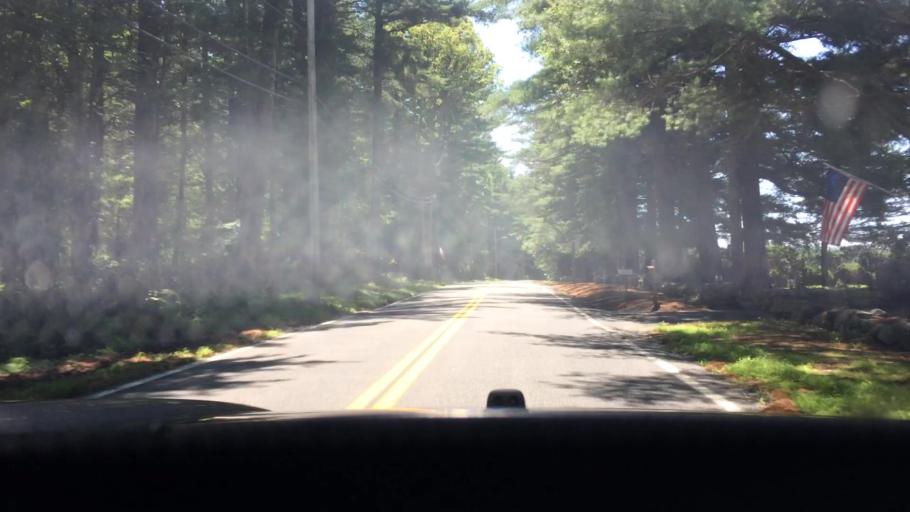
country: US
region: Rhode Island
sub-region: Providence County
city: Harrisville
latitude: 41.9922
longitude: -71.6835
